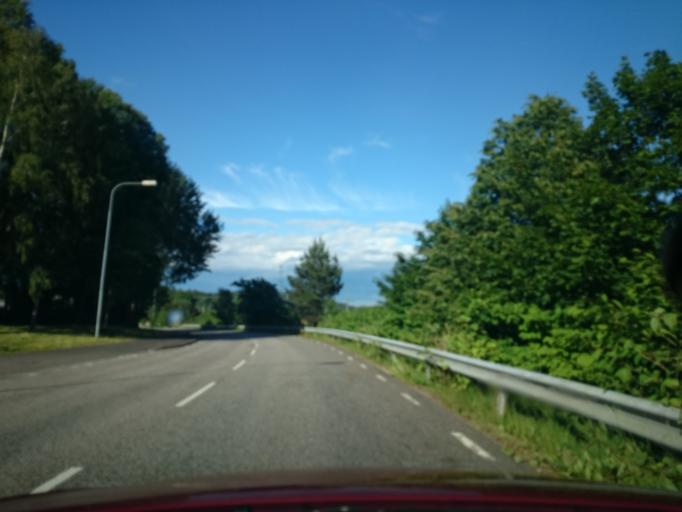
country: SE
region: Vaestra Goetaland
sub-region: Lerums Kommun
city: Stenkullen
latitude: 57.7928
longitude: 12.3154
